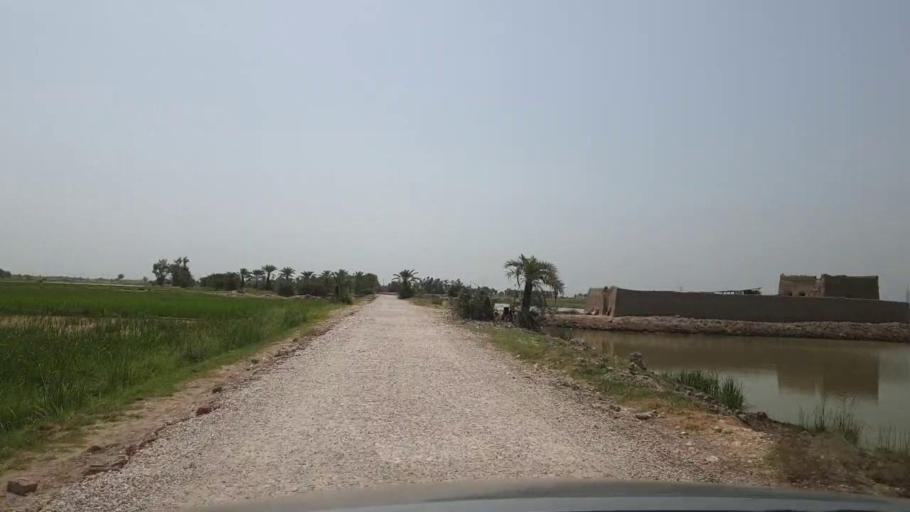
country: PK
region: Sindh
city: Garhi Yasin
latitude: 27.8989
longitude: 68.4956
